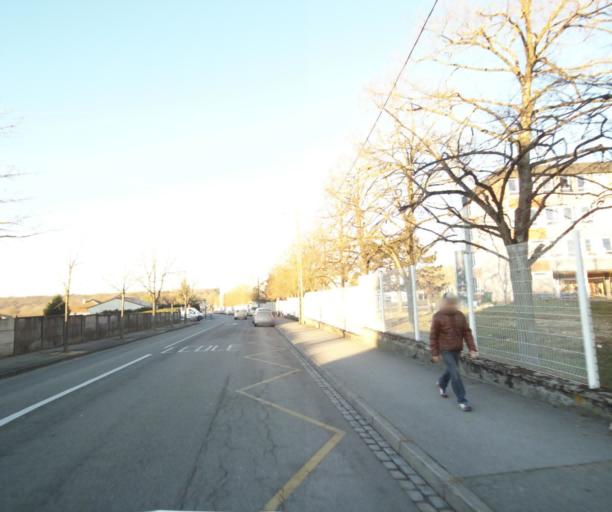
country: FR
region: Lorraine
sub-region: Departement de Meurthe-et-Moselle
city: Laxou
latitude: 48.6906
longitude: 6.1382
